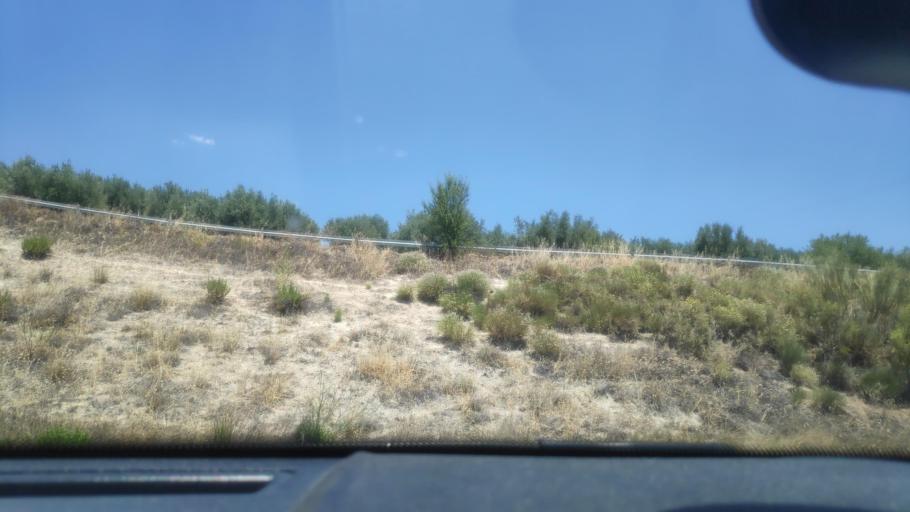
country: ES
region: Andalusia
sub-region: Provincia de Granada
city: Campotejar
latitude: 37.4877
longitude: -3.6014
